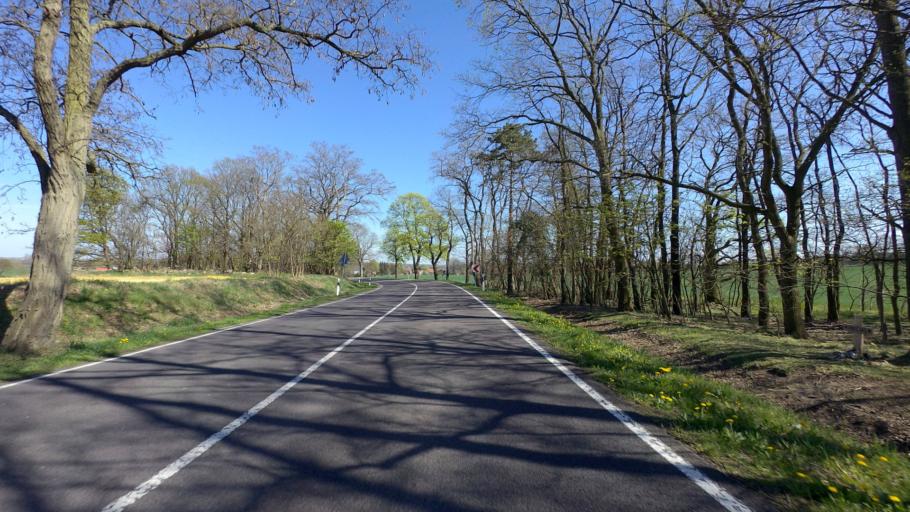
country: DE
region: Saxony-Anhalt
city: Kalbe
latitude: 52.6457
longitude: 11.3302
